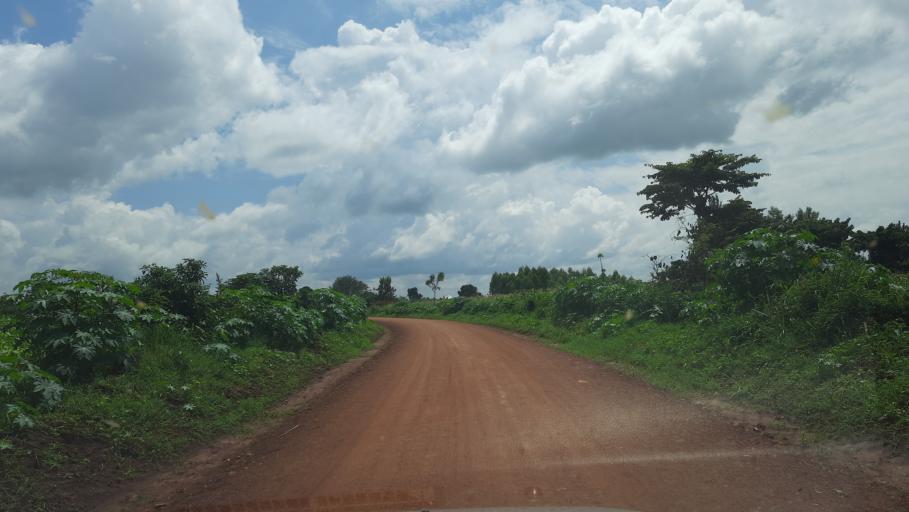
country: UG
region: Western Region
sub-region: Kiryandongo District
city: Kiryandongo
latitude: 1.8220
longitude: 31.9834
